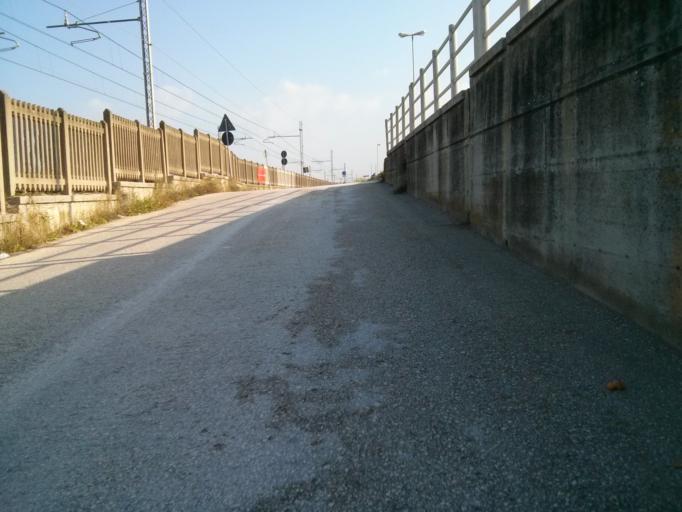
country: IT
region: The Marches
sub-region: Provincia di Pesaro e Urbino
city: Fenile
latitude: 43.8806
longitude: 12.9625
